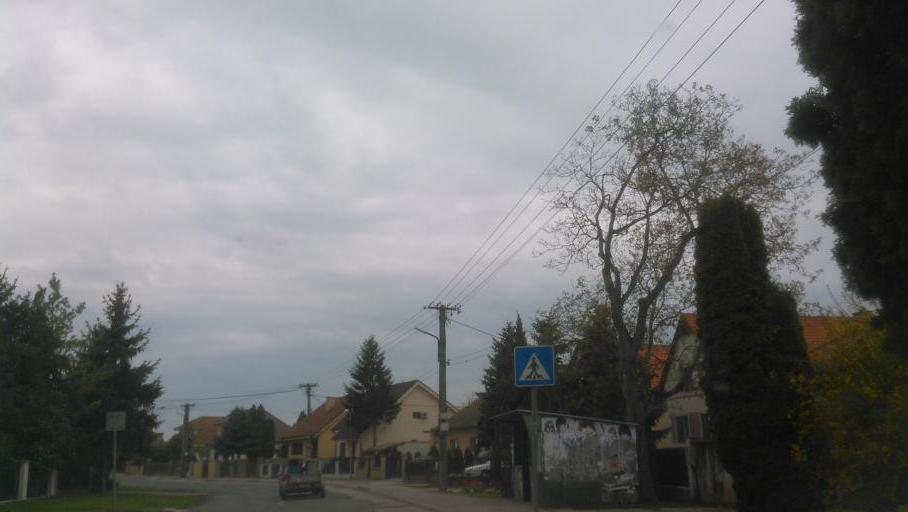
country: SK
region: Bratislavsky
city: Senec
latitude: 48.1475
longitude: 17.3383
